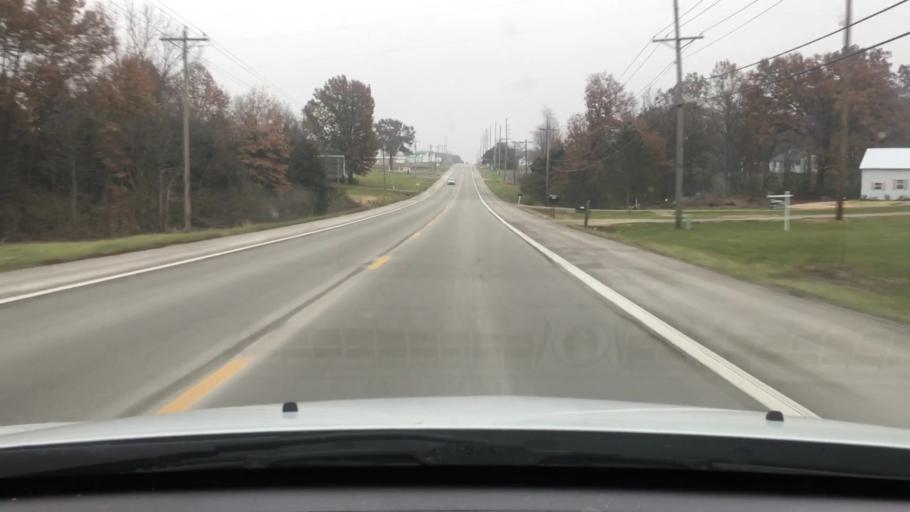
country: US
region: Missouri
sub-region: Audrain County
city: Mexico
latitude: 39.1634
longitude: -91.8369
